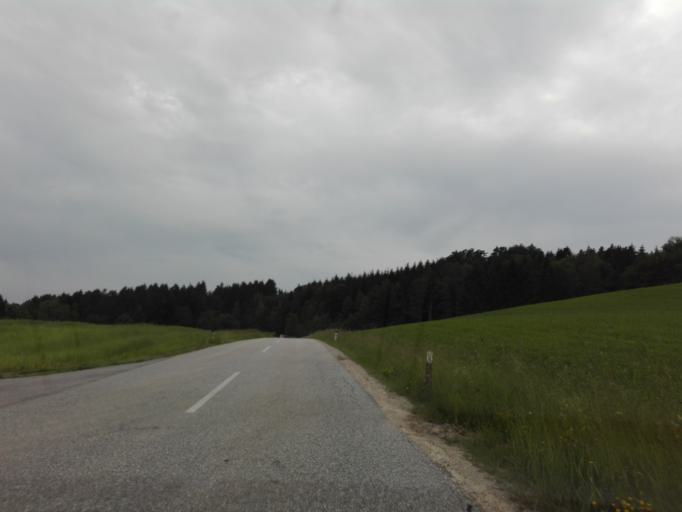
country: AT
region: Upper Austria
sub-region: Politischer Bezirk Perg
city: Bad Kreuzen
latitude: 48.2865
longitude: 14.7380
